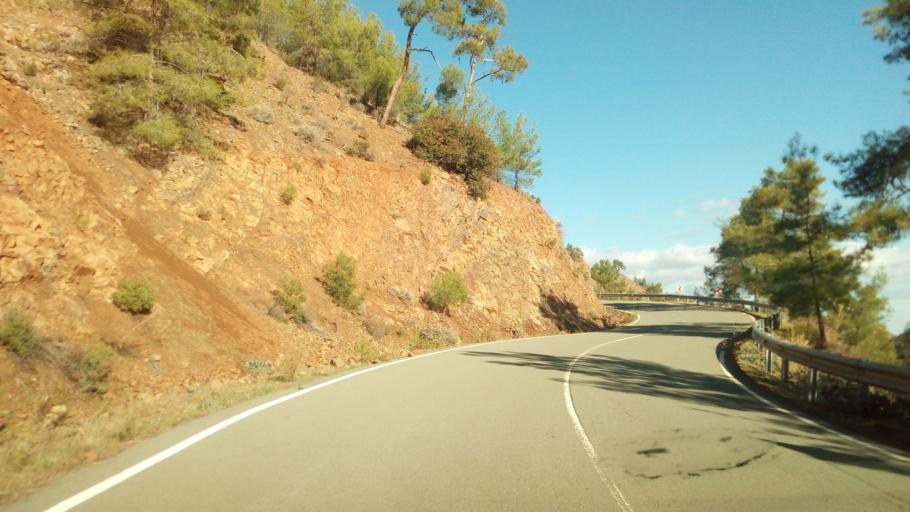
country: CY
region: Lefkosia
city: Lefka
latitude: 35.0954
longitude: 32.7579
